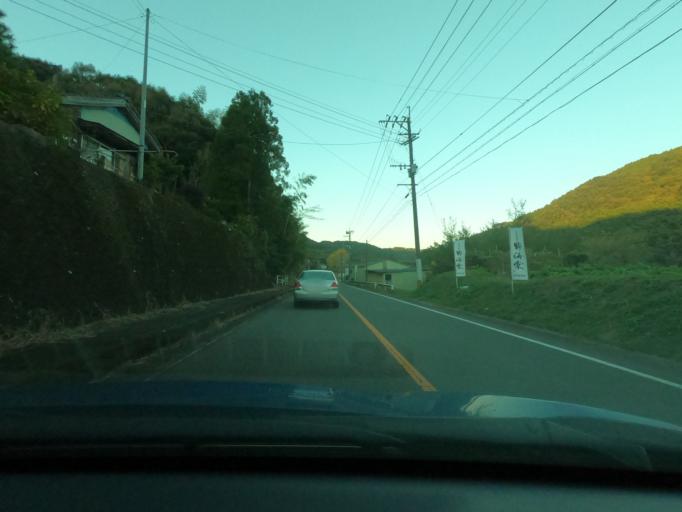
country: JP
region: Kagoshima
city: Satsumasendai
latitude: 31.8031
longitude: 130.4807
